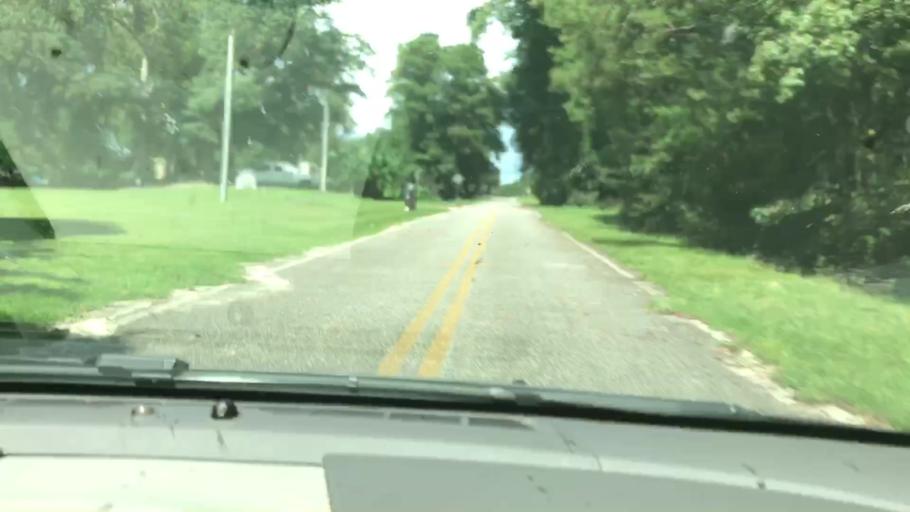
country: US
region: Georgia
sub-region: Clay County
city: Fort Gaines
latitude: 31.7317
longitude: -85.0931
